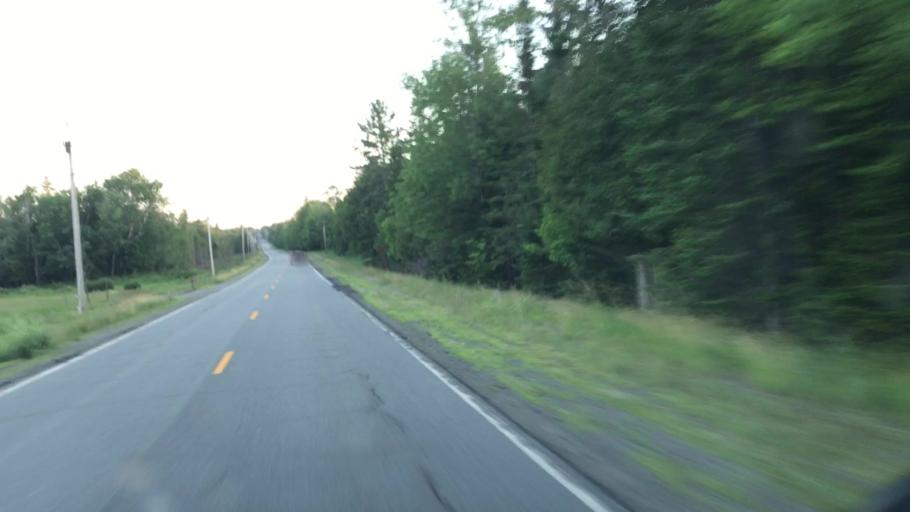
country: US
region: Maine
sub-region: Penobscot County
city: Medway
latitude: 45.6114
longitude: -68.3052
